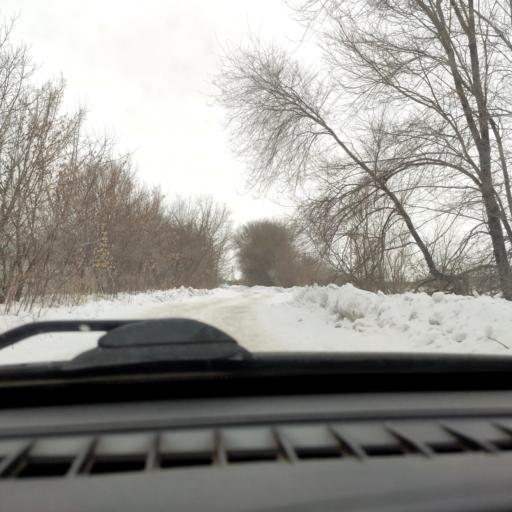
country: RU
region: Samara
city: Tol'yatti
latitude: 53.5678
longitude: 49.4730
